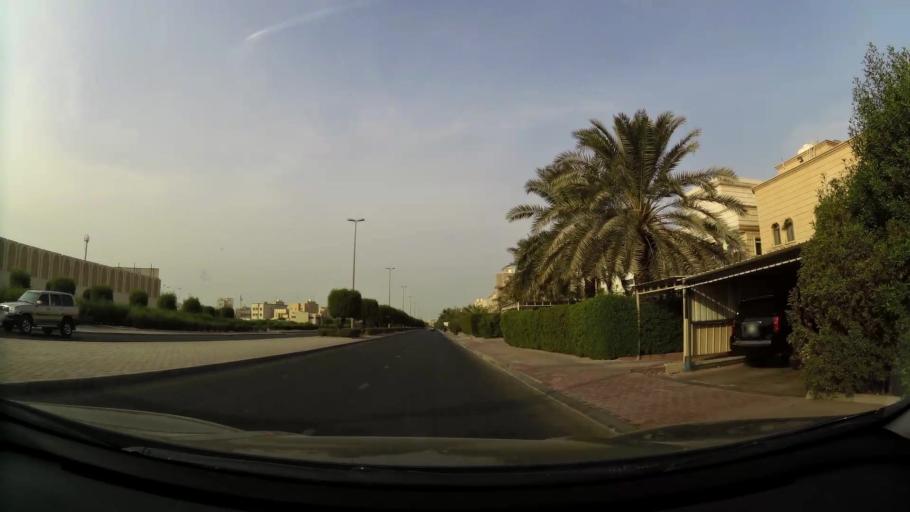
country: KW
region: Mubarak al Kabir
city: Mubarak al Kabir
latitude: 29.1893
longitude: 48.0807
